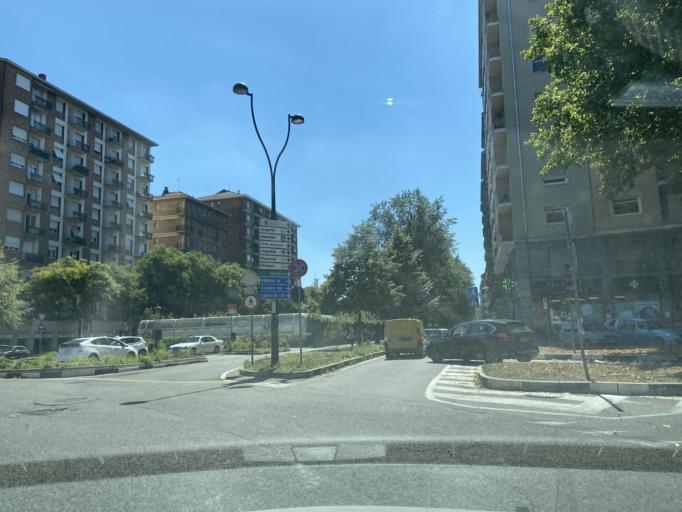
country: IT
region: Piedmont
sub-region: Provincia di Torino
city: Lesna
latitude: 45.0755
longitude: 7.6430
